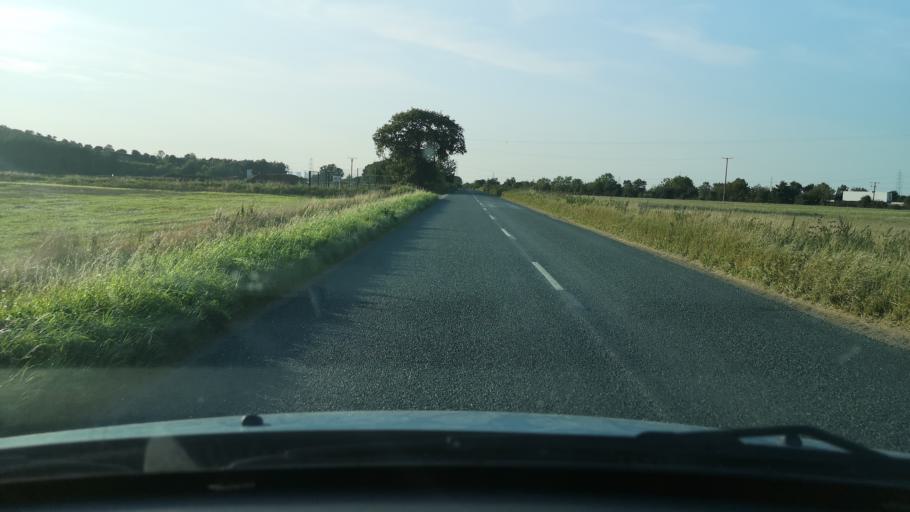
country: GB
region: England
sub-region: Doncaster
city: Norton
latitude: 53.6925
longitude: -1.1713
